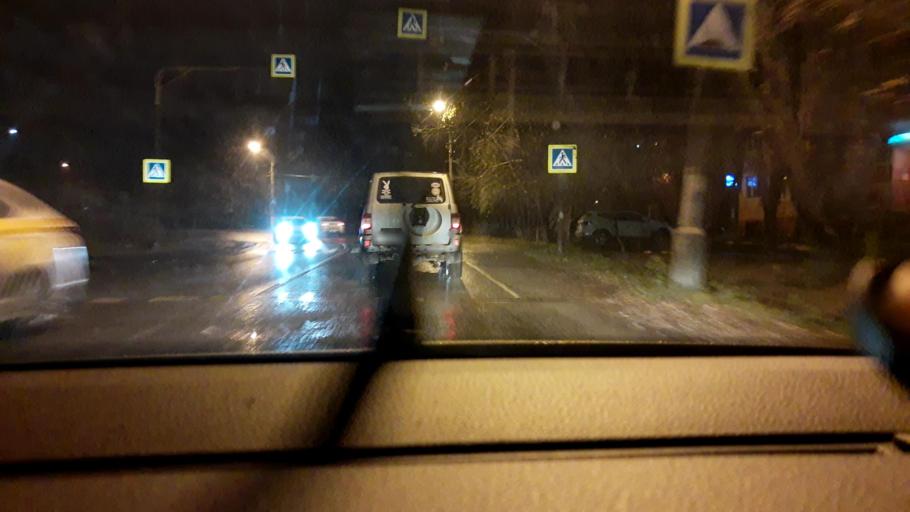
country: RU
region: Moskovskaya
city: Shchelkovo
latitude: 55.9296
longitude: 37.9823
